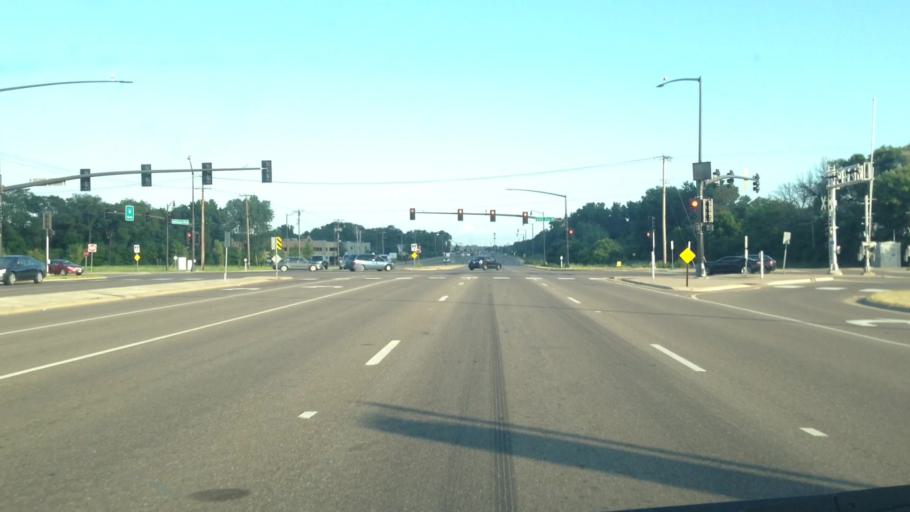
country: US
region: Minnesota
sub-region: Hennepin County
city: Brooklyn Park
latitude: 45.0699
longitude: -93.3685
